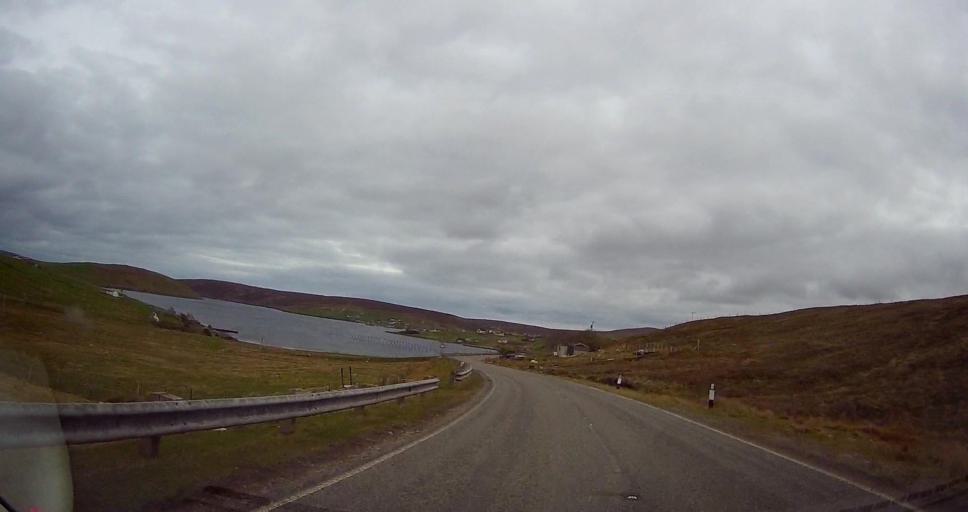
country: GB
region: Scotland
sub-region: Shetland Islands
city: Shetland
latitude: 60.6143
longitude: -1.0749
